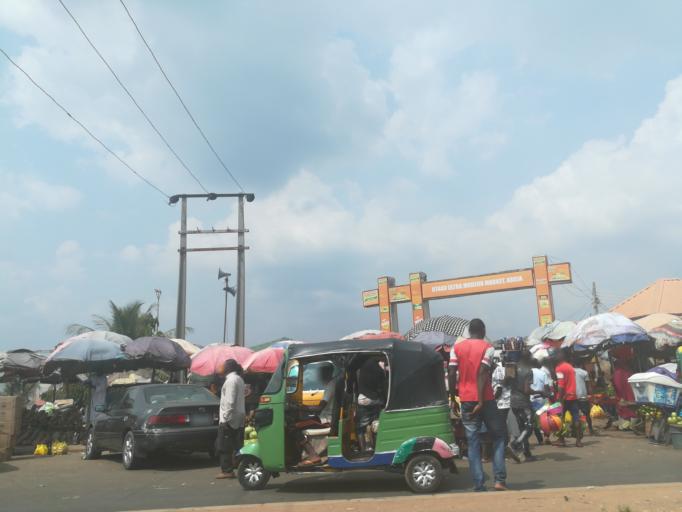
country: NG
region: Abuja Federal Capital Territory
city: Abuja
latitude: 9.0643
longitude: 7.4464
